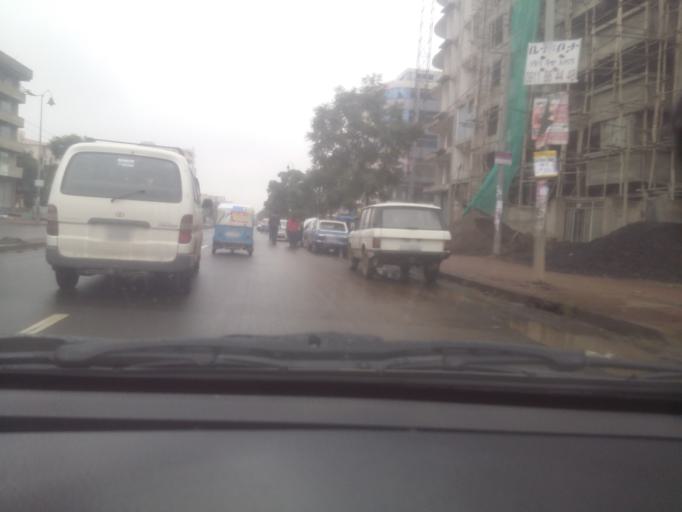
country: ET
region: Adis Abeba
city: Addis Ababa
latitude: 8.9492
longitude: 38.7215
